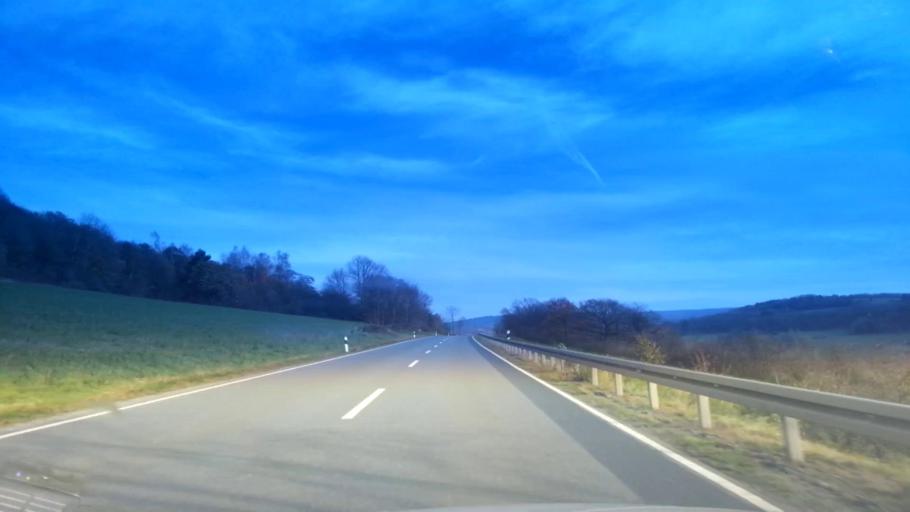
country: DE
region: Bavaria
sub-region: Upper Franconia
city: Neunkirchen am Main
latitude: 49.9599
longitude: 11.6515
